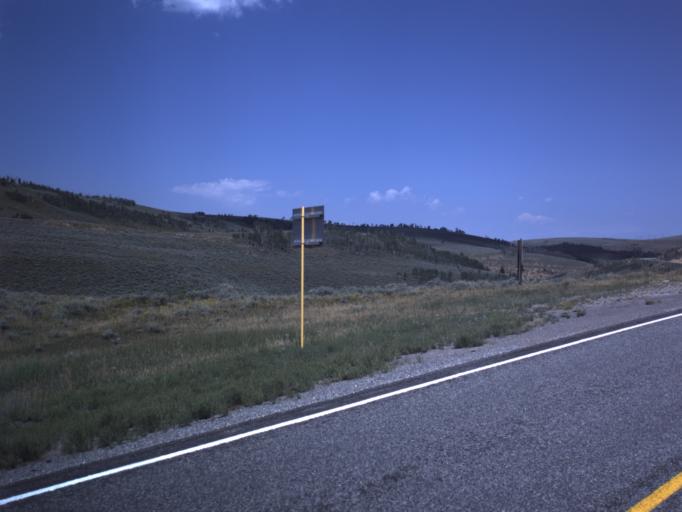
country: US
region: Utah
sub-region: Carbon County
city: Helper
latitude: 39.8204
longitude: -111.1353
